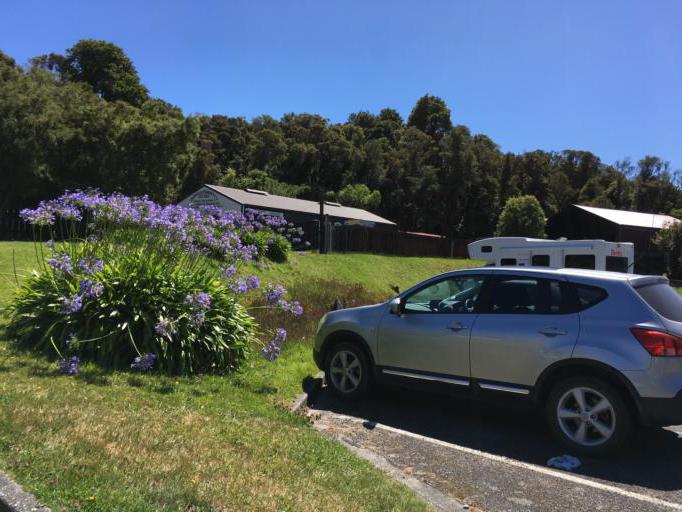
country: NZ
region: West Coast
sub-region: Grey District
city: Greymouth
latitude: -42.5347
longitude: 171.1822
